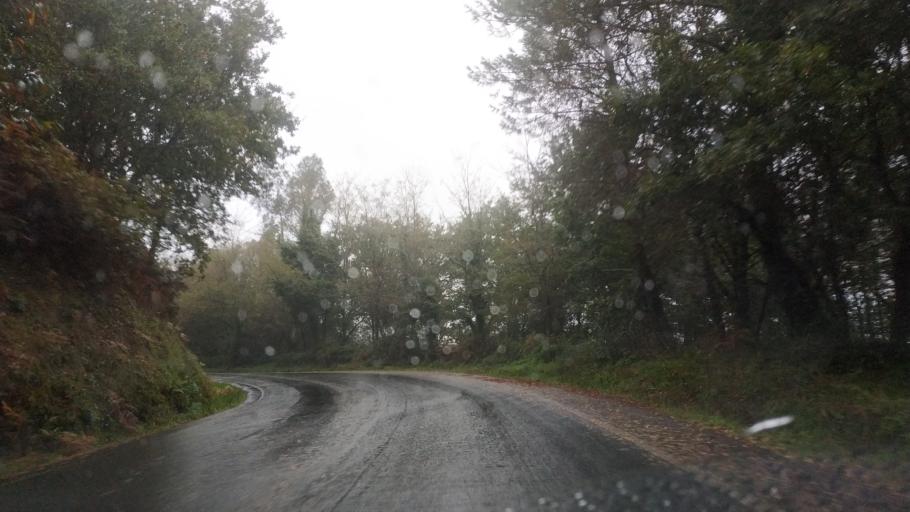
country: ES
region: Galicia
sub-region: Provincia da Coruna
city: Negreira
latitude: 42.9084
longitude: -8.7480
